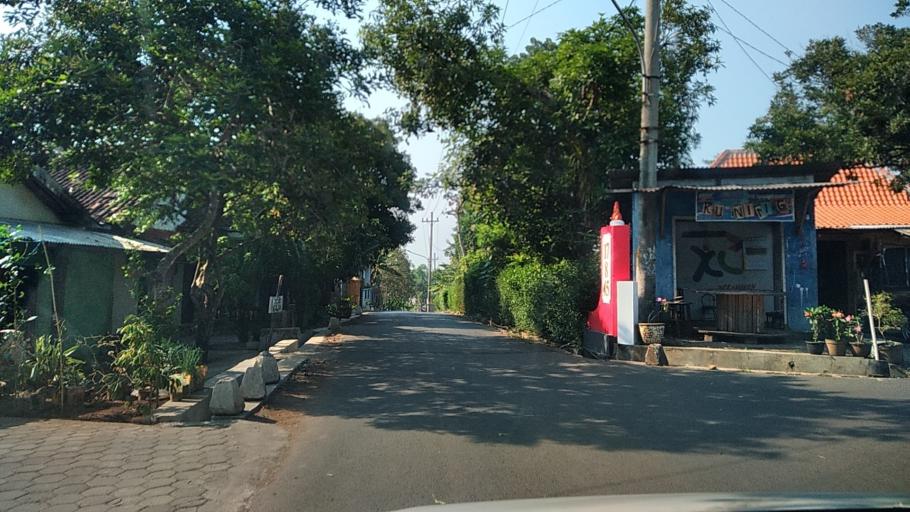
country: ID
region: Central Java
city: Semarang
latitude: -7.0287
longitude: 110.3428
